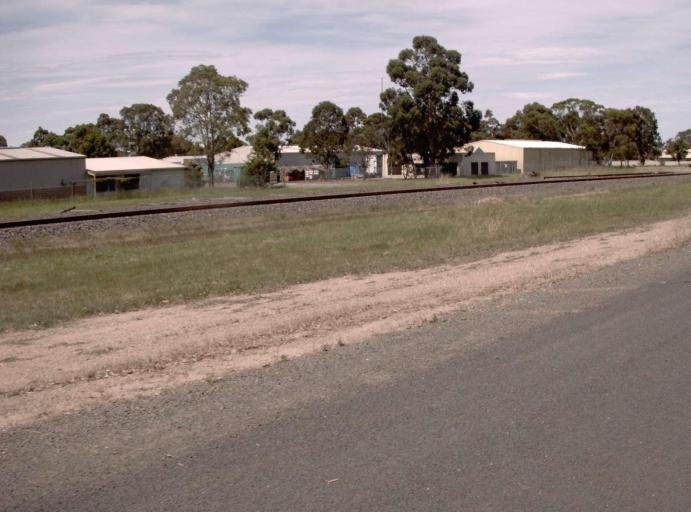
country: AU
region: Victoria
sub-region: Wellington
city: Sale
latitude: -38.1043
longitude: 147.0281
